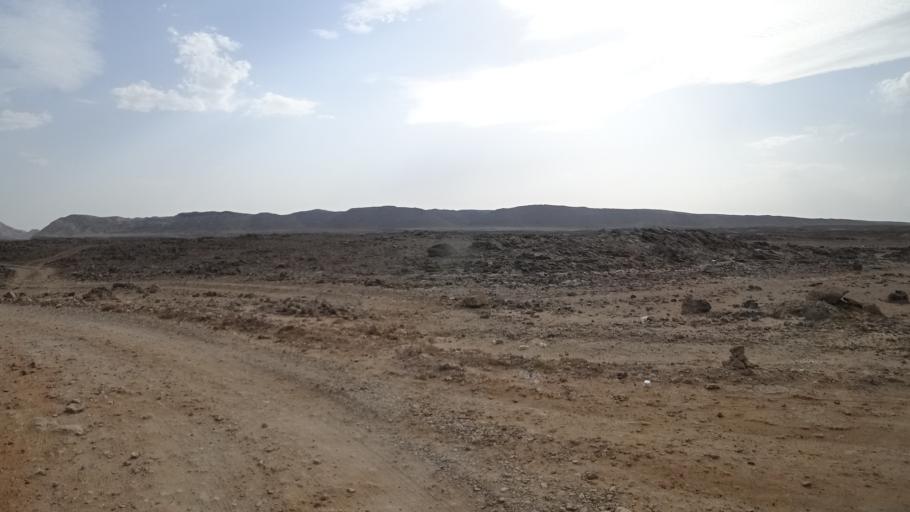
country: OM
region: Ash Sharqiyah
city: Sur
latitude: 22.4525
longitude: 59.8251
